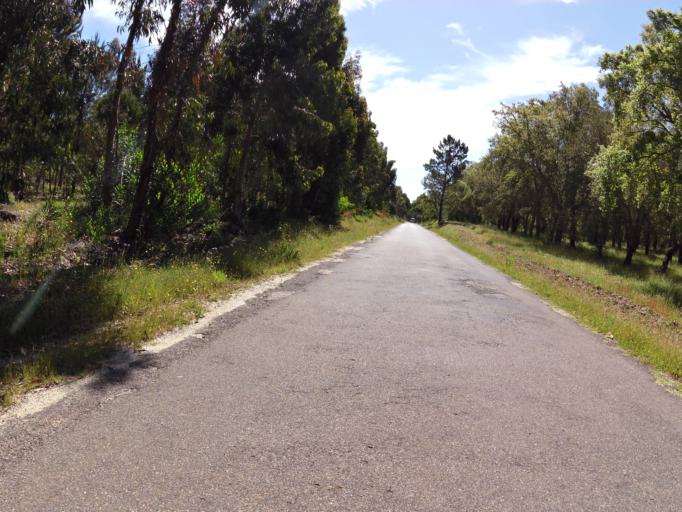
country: PT
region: Setubal
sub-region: Sines
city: Porto Covo
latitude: 37.9366
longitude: -8.7658
